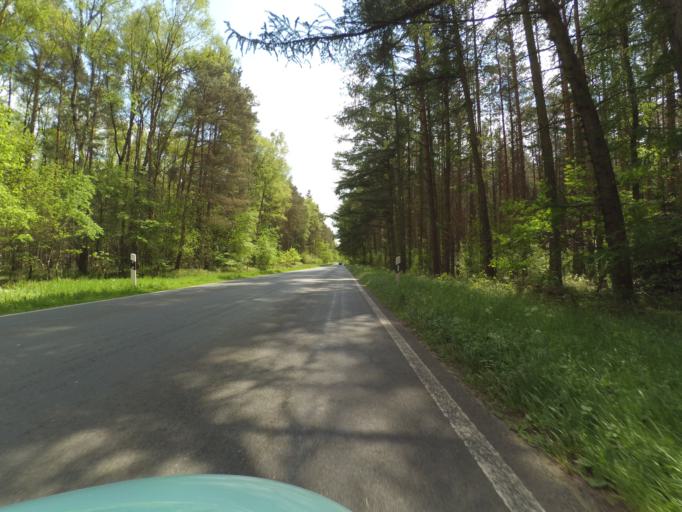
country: DE
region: Lower Saxony
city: Hambuhren
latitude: 52.6115
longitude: 9.9829
